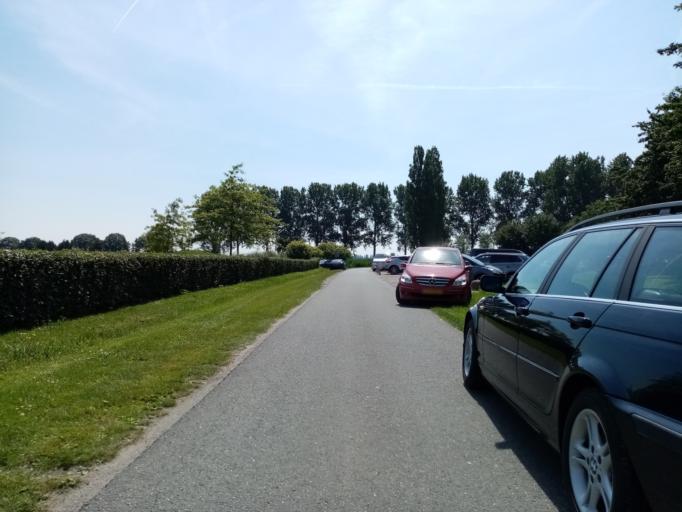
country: NL
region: South Holland
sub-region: Gemeente Nieuwkoop
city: Nieuwkoop
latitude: 52.1858
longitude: 4.7407
